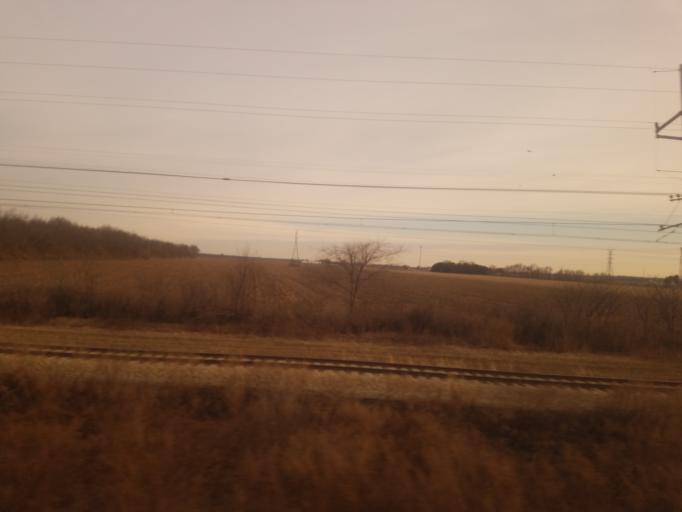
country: US
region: Indiana
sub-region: Saint Joseph County
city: New Carlisle
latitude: 41.7012
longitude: -86.4566
